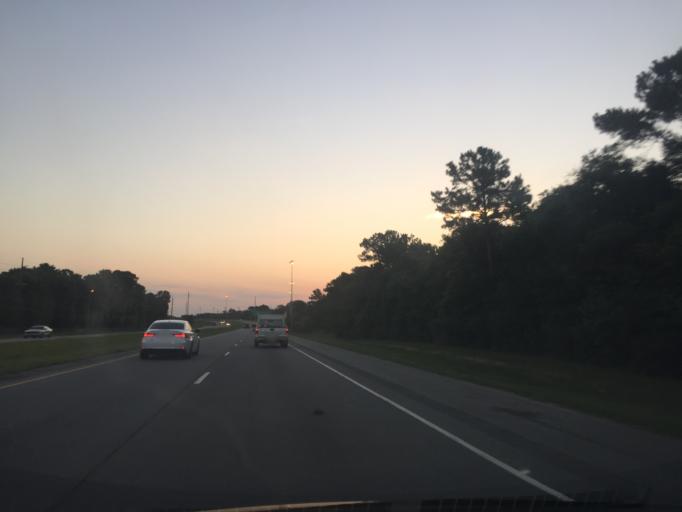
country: US
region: Georgia
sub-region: Chatham County
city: Isle of Hope
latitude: 31.9845
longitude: -81.0878
